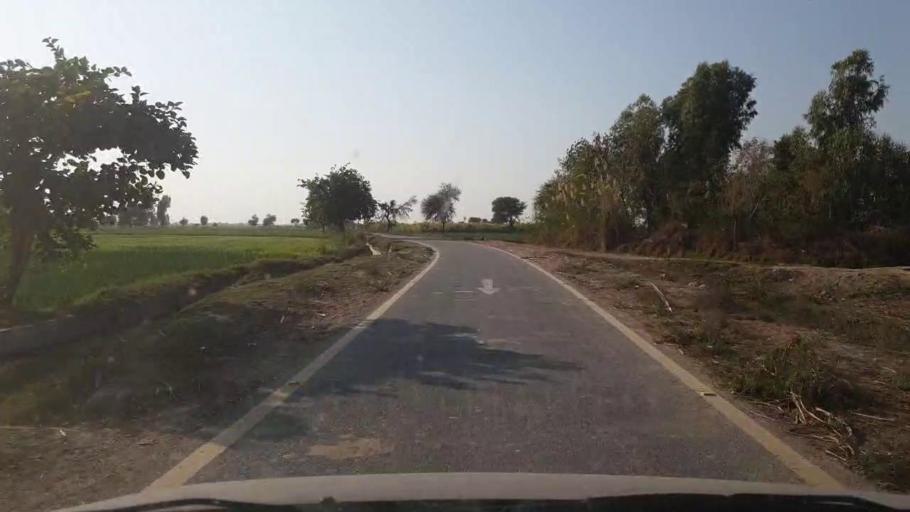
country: PK
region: Sindh
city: Samaro
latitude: 25.2881
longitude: 69.3546
